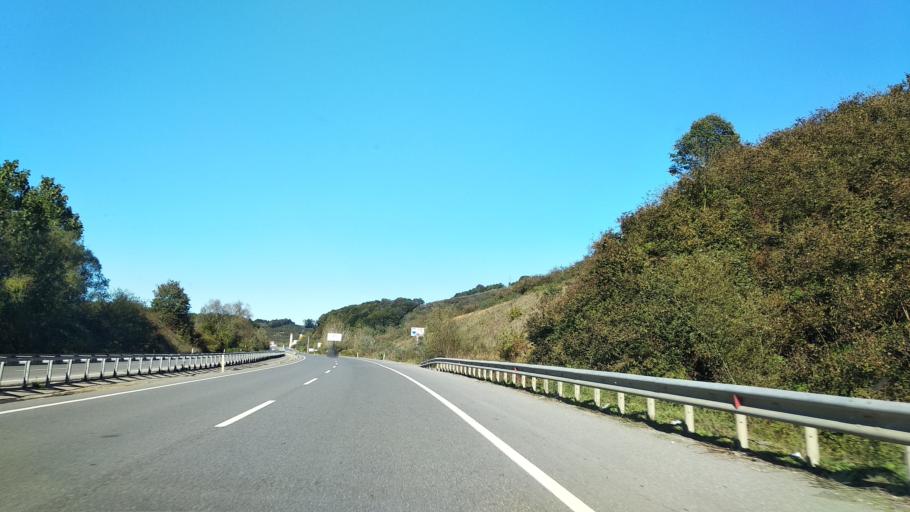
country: TR
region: Sakarya
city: Karasu
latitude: 41.0662
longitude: 30.6429
